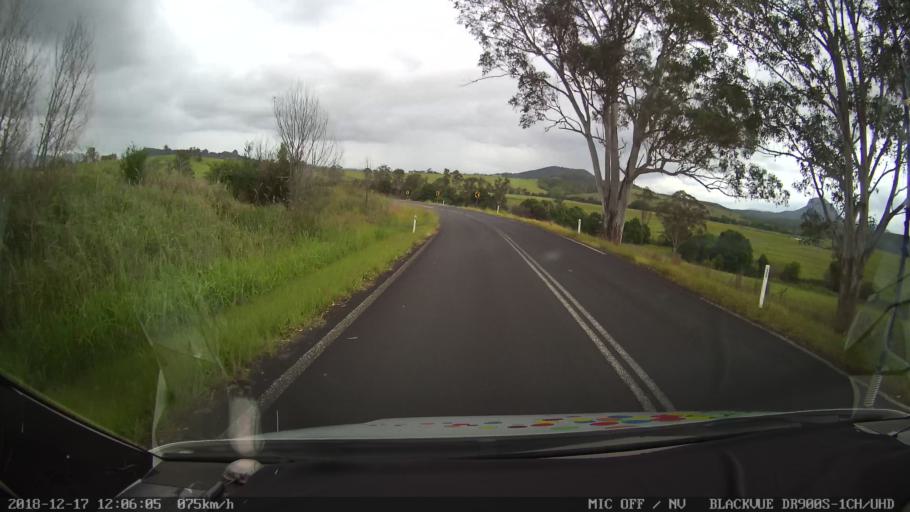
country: AU
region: New South Wales
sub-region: Kyogle
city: Kyogle
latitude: -28.4861
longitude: 152.5684
